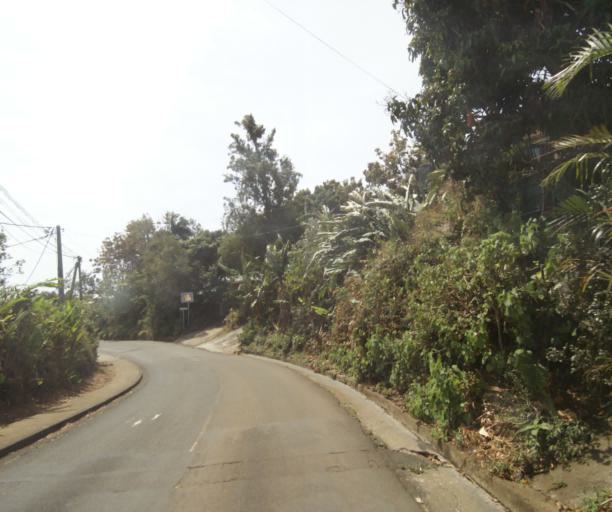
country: RE
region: Reunion
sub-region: Reunion
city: Trois-Bassins
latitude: -21.0720
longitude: 55.2930
